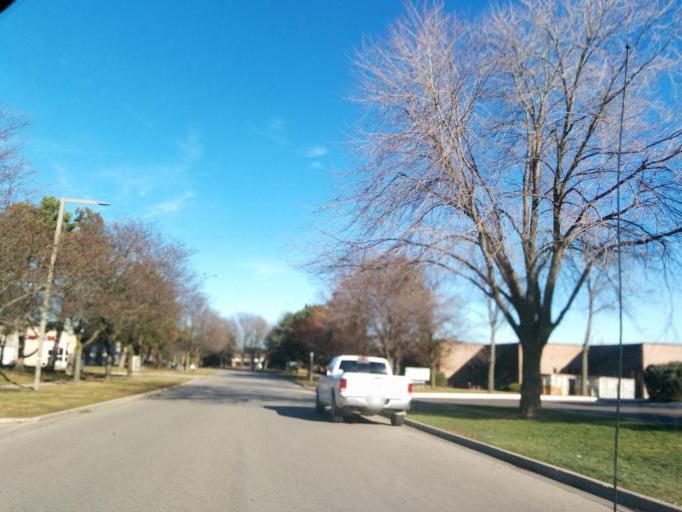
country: CA
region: Ontario
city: Mississauga
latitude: 43.5294
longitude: -79.6808
